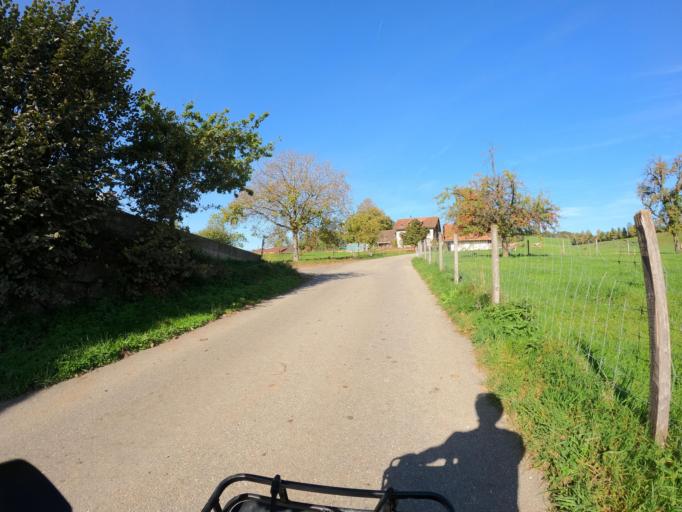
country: CH
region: Zug
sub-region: Zug
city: Baar
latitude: 47.2157
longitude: 8.5560
